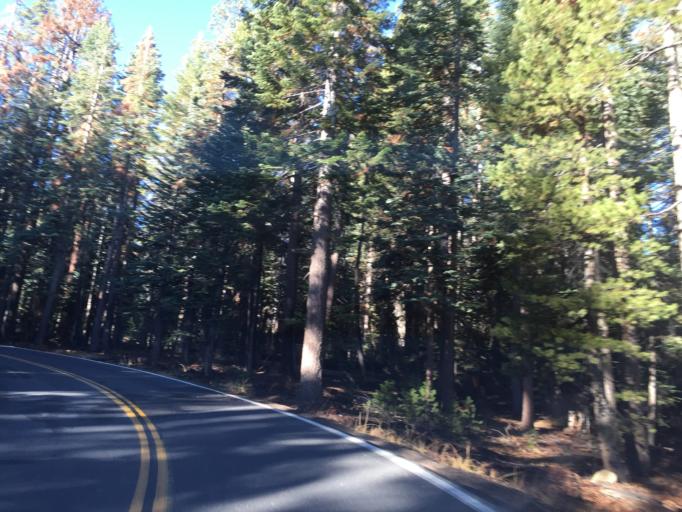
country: US
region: California
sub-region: Mariposa County
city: Yosemite Valley
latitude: 37.7209
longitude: -119.5794
